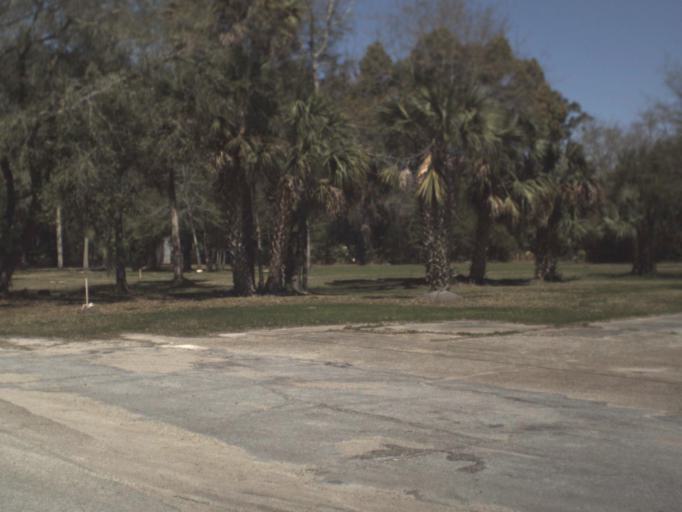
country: US
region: Florida
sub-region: Leon County
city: Woodville
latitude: 30.1583
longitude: -84.2049
